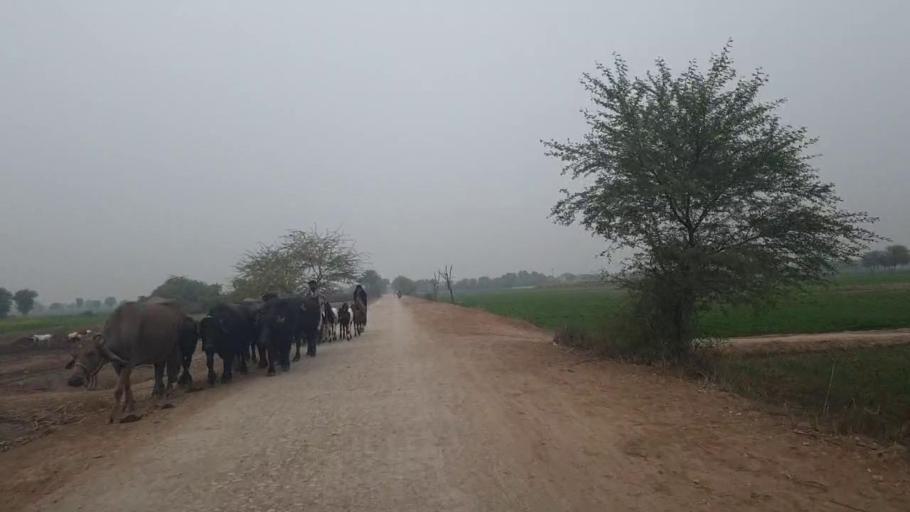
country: PK
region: Sindh
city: Tando Adam
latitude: 25.7749
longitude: 68.6985
